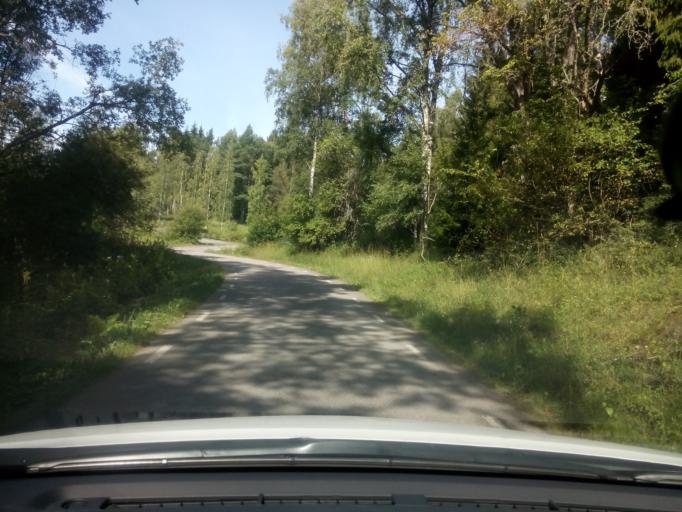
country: SE
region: Soedermanland
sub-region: Trosa Kommun
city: Trosa
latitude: 58.7962
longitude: 17.3812
